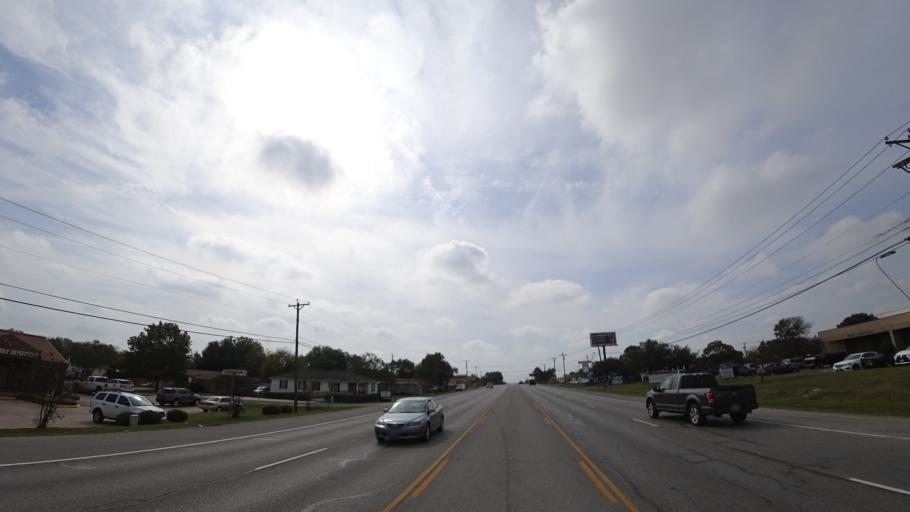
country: US
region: Texas
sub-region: Travis County
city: Wells Branch
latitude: 30.4462
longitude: -97.6633
